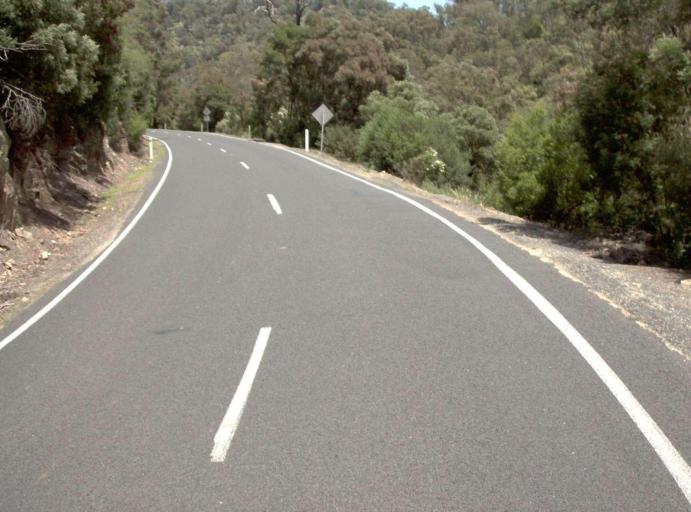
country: AU
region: Victoria
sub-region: East Gippsland
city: Lakes Entrance
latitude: -37.5501
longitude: 147.8740
